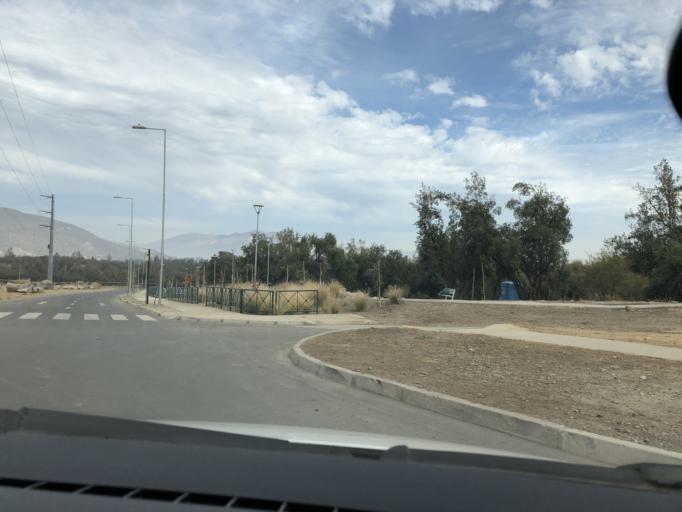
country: CL
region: Santiago Metropolitan
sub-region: Provincia de Cordillera
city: Puente Alto
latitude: -33.5834
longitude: -70.5167
